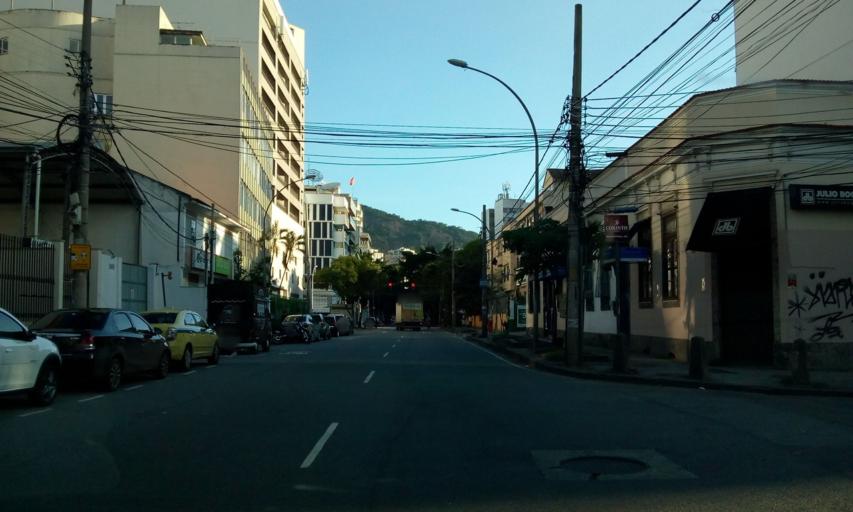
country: BR
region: Rio de Janeiro
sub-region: Rio De Janeiro
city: Rio de Janeiro
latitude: -22.9467
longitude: -43.1841
